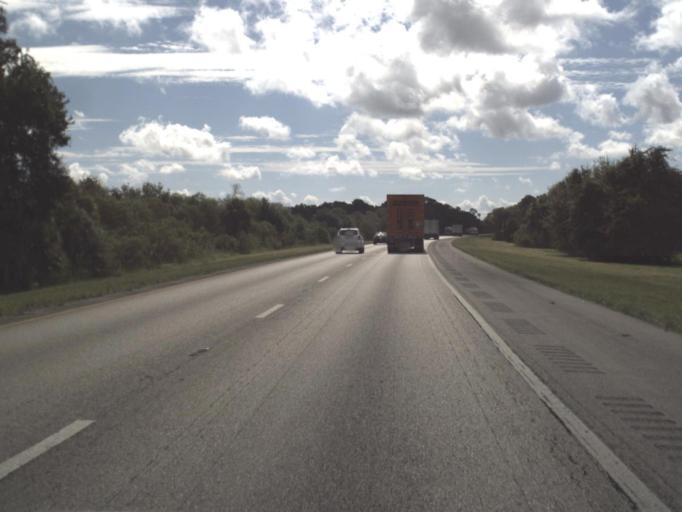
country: US
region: Florida
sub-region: Sarasota County
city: North Port
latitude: 27.0961
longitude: -82.1282
